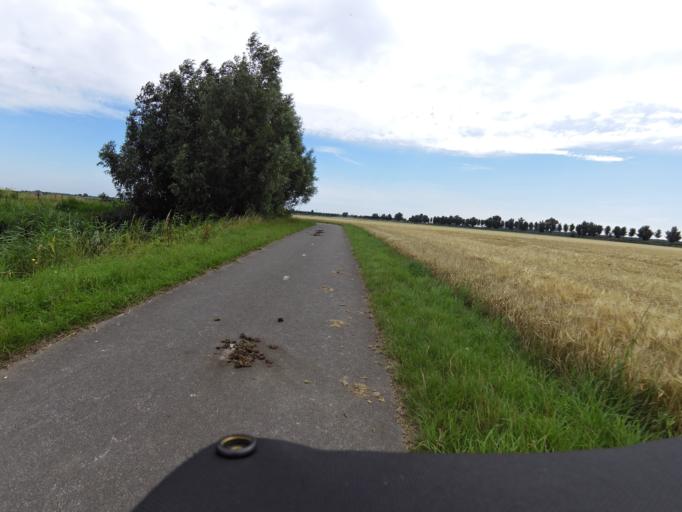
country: NL
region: South Holland
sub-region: Gemeente Strijen
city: Strijen
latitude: 51.7277
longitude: 4.5348
